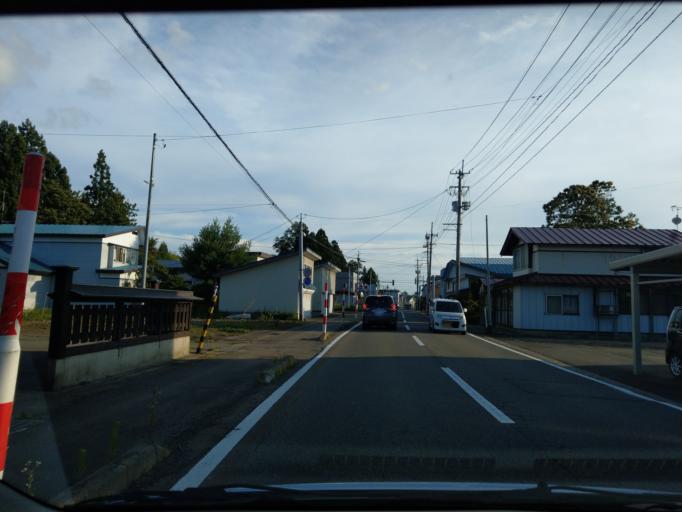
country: JP
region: Akita
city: Omagari
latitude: 39.4369
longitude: 140.5630
